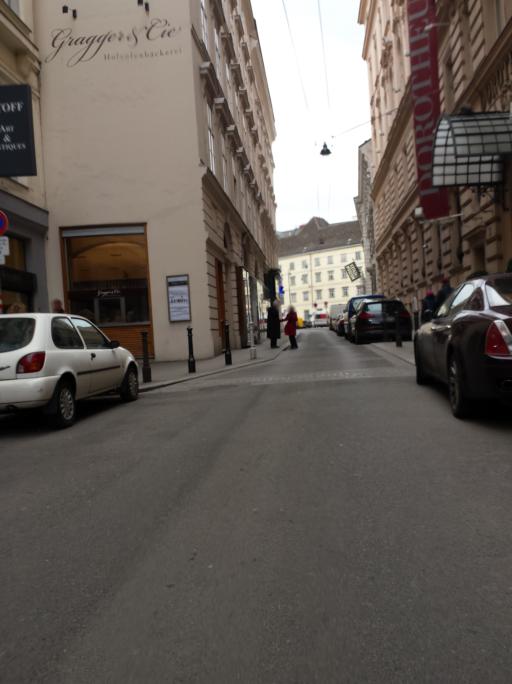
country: AT
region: Vienna
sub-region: Wien Stadt
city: Vienna
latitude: 48.2064
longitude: 16.3694
